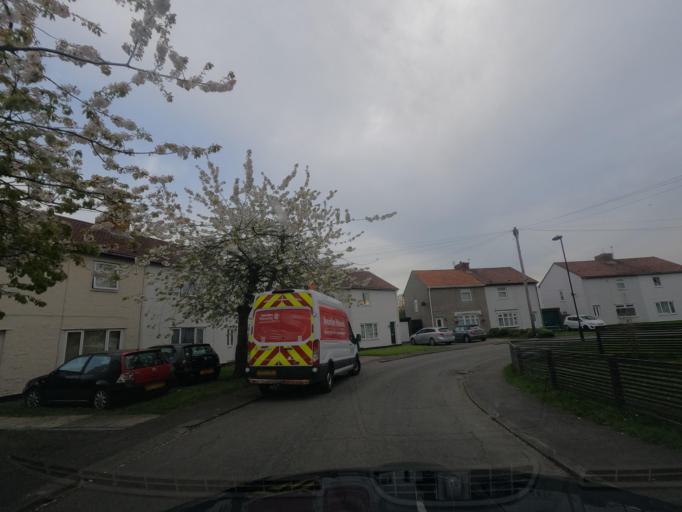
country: GB
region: England
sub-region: Northumberland
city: Backworth
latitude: 55.0414
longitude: -1.5374
